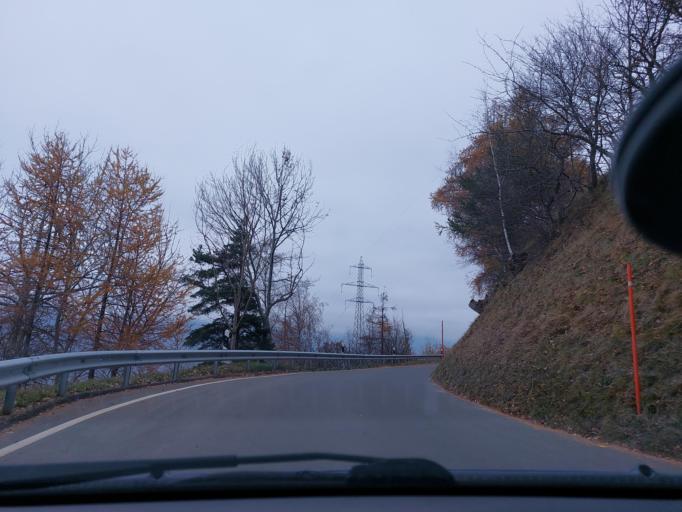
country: CH
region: Valais
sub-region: Martigny District
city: Riddes
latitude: 46.1743
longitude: 7.2501
